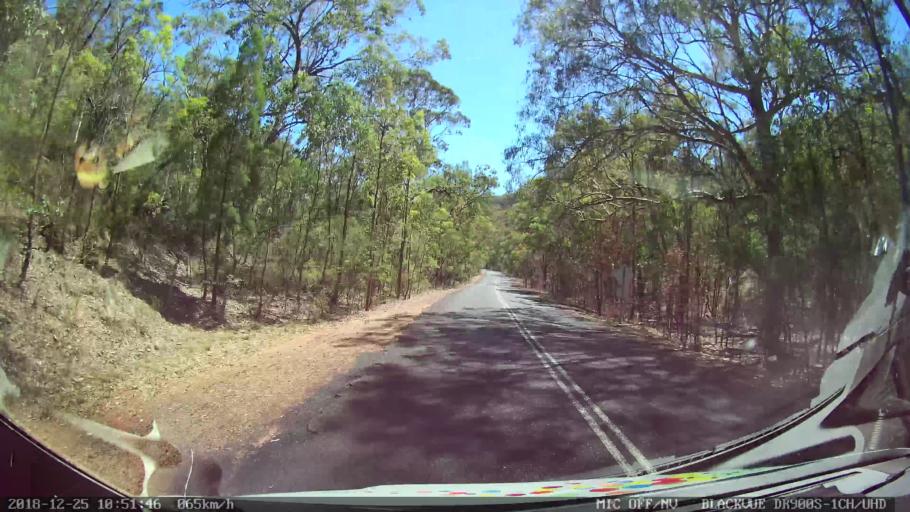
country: AU
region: New South Wales
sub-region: Upper Hunter Shire
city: Merriwa
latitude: -32.4342
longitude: 150.2705
